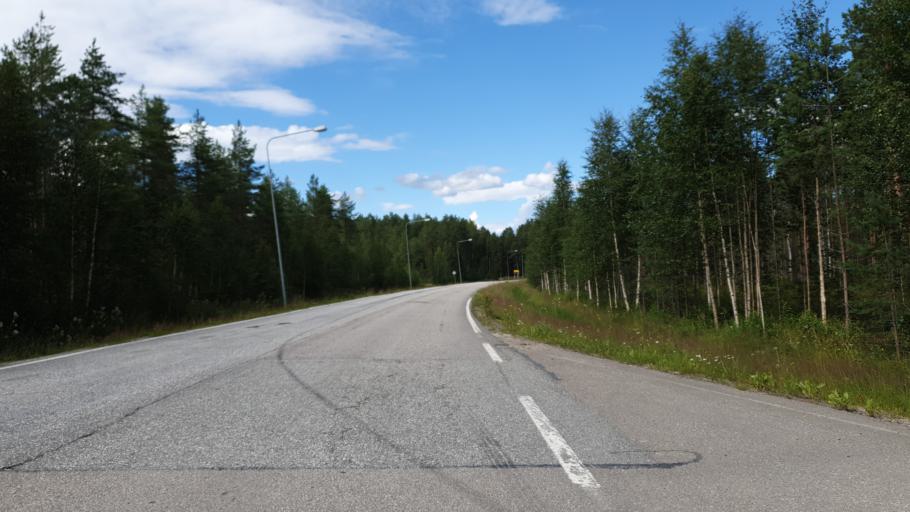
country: FI
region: Kainuu
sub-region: Kehys-Kainuu
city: Kuhmo
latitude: 64.1162
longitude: 29.5271
